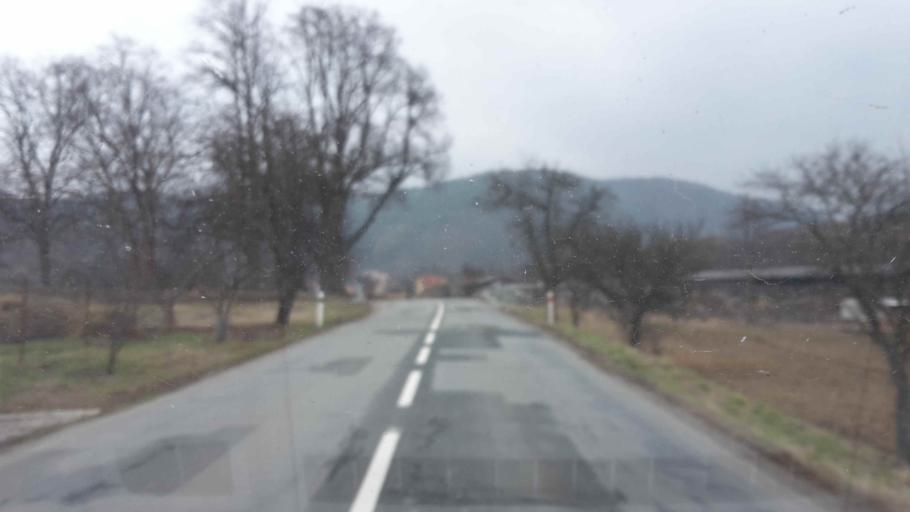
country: CZ
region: South Moravian
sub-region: Okres Brno-Venkov
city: Dolni Loucky
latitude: 49.3942
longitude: 16.3676
